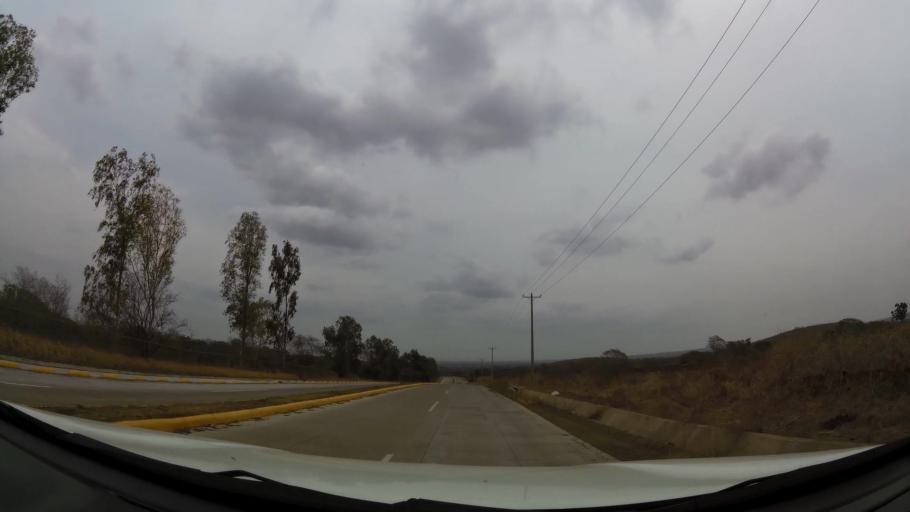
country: NI
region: Masaya
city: Ticuantepe
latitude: 12.0920
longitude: -86.1813
